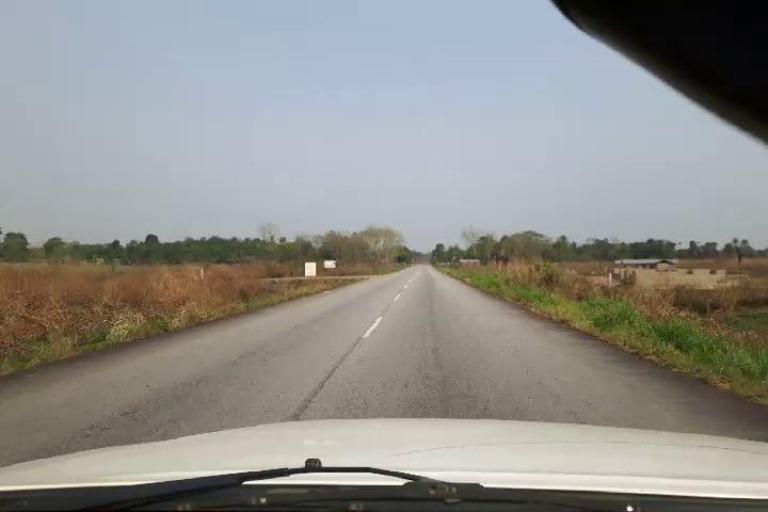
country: SL
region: Southern Province
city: Baiima
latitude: 8.1443
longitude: -11.9021
